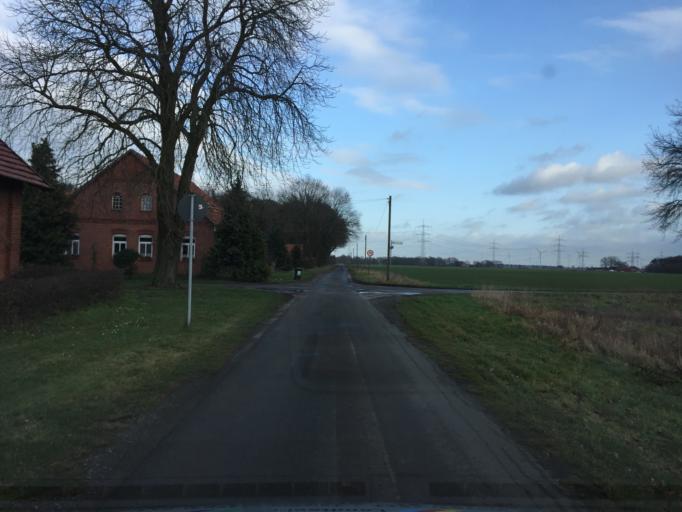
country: DE
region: Lower Saxony
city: Steyerberg
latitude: 52.5401
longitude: 9.0135
